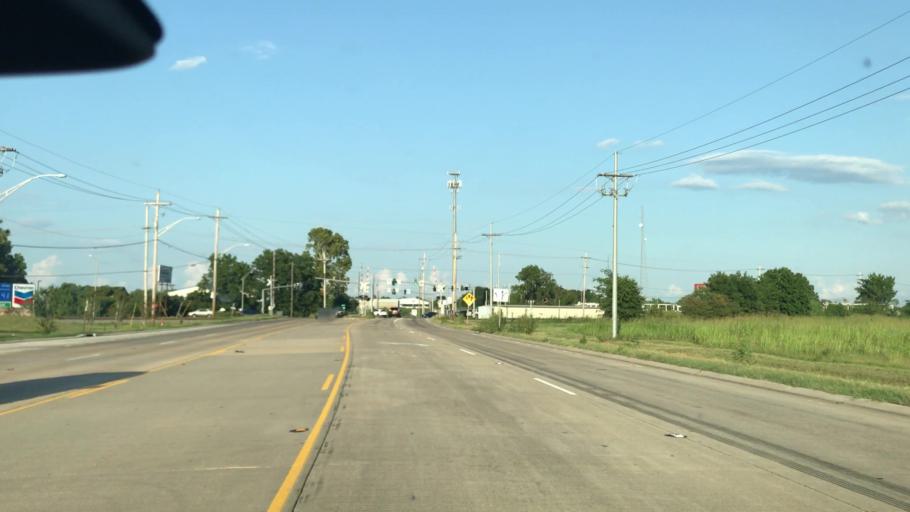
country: US
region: Louisiana
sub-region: Bossier Parish
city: Bossier City
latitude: 32.4008
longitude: -93.6952
